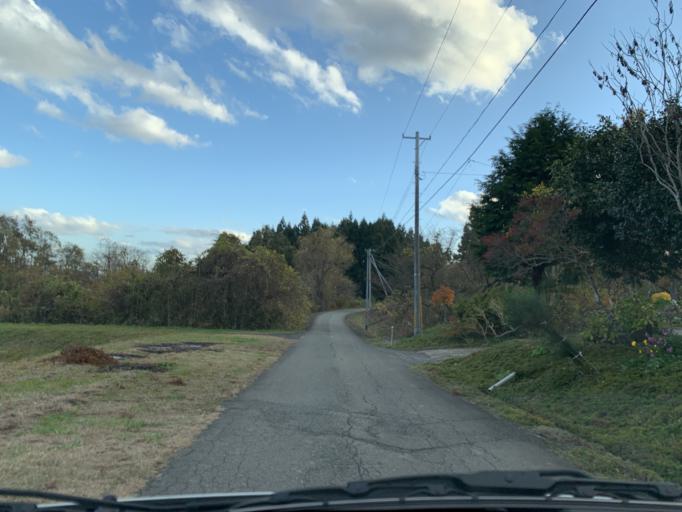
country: JP
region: Iwate
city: Mizusawa
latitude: 39.1094
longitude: 141.0392
